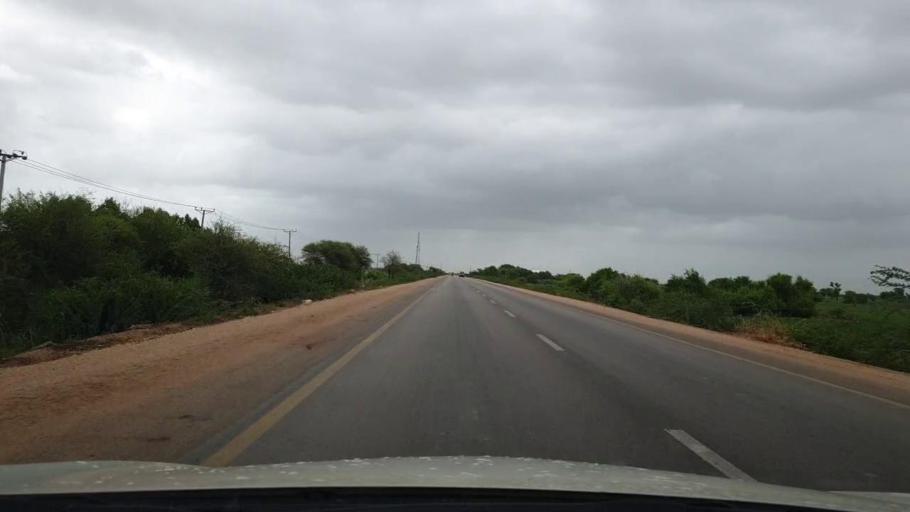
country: PK
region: Sindh
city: Badin
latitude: 24.6552
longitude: 68.7383
